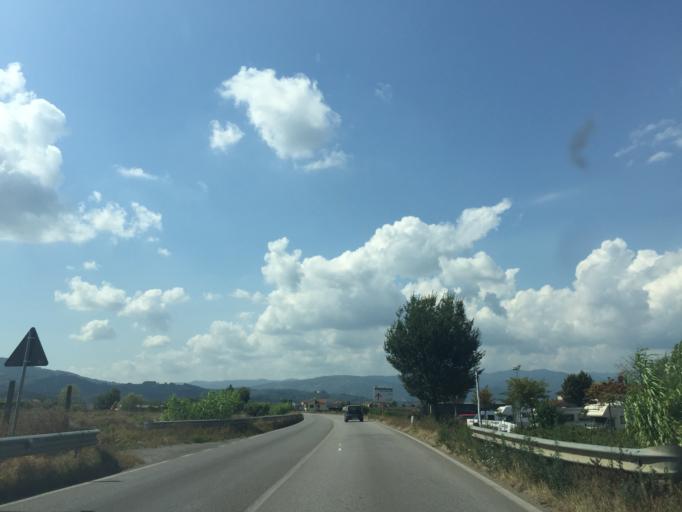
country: IT
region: Tuscany
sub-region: Provincia di Pistoia
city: Cantagrillo-Casalguidi
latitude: 43.8796
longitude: 10.9246
